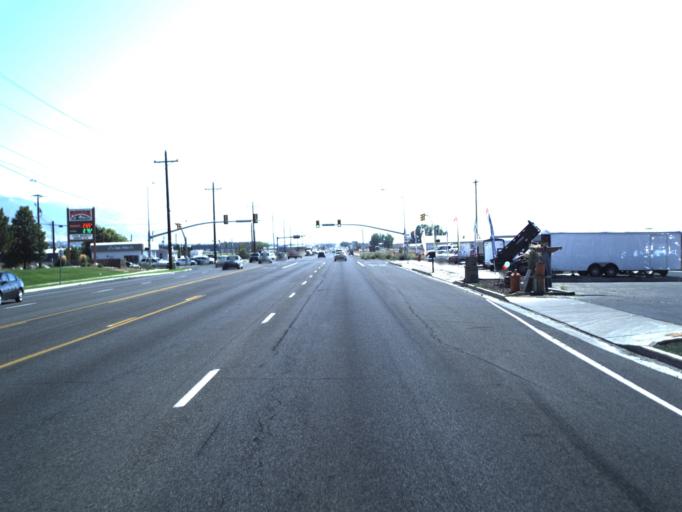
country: US
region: Utah
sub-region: Cache County
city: Hyde Park
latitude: 41.8005
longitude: -111.8336
